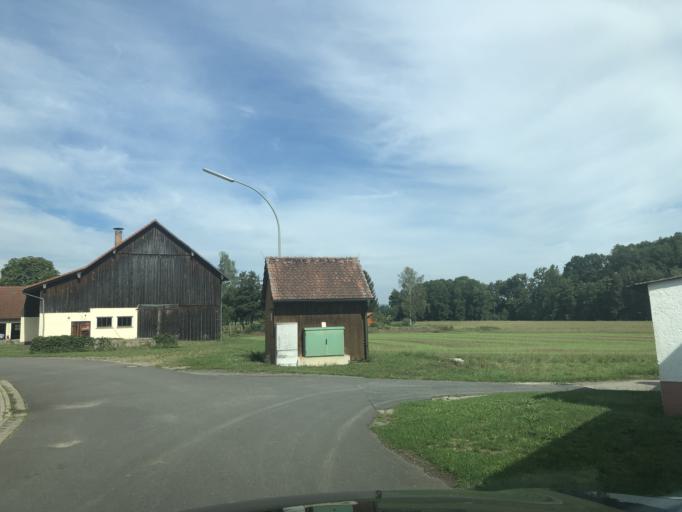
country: DE
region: Bavaria
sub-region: Upper Palatinate
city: Trabitz
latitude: 49.7904
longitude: 11.8923
